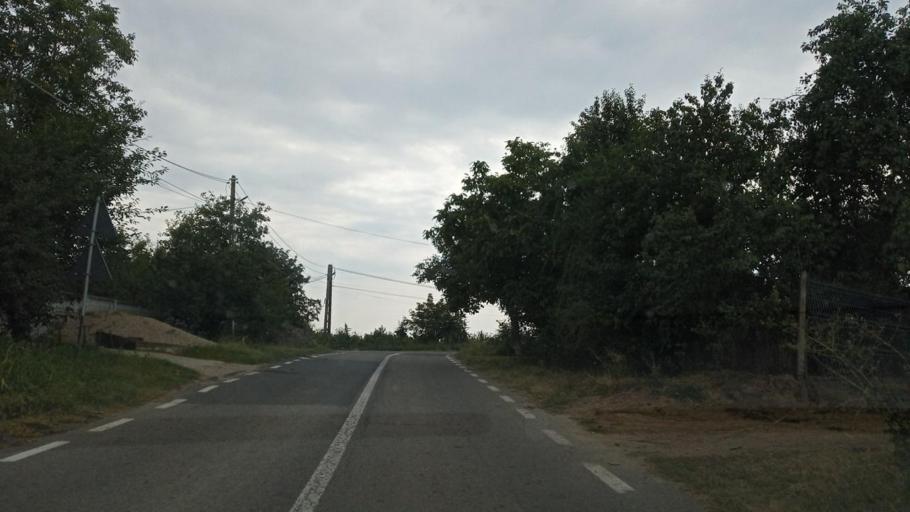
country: RO
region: Giurgiu
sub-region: Comuna Izvoarele
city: Isvoarele
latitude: 44.1677
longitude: 26.2869
